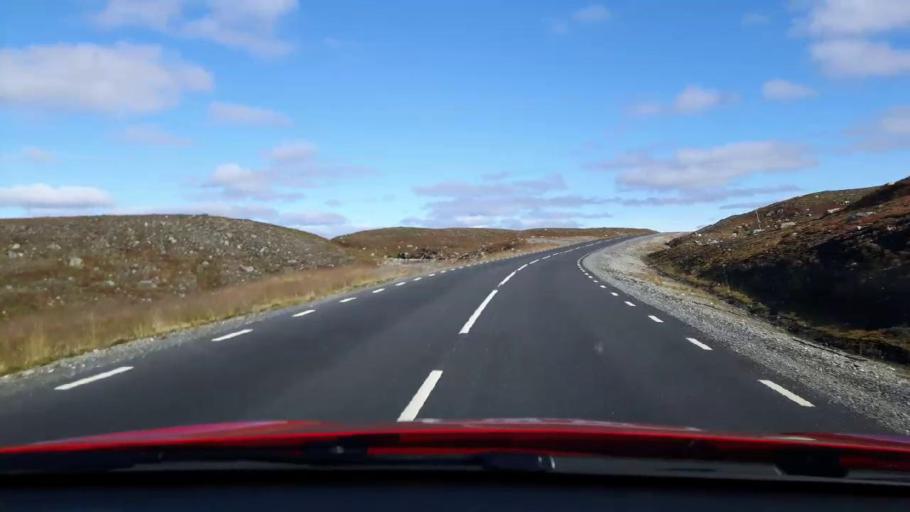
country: NO
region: Nordland
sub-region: Hattfjelldal
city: Hattfjelldal
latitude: 65.0538
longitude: 14.3490
